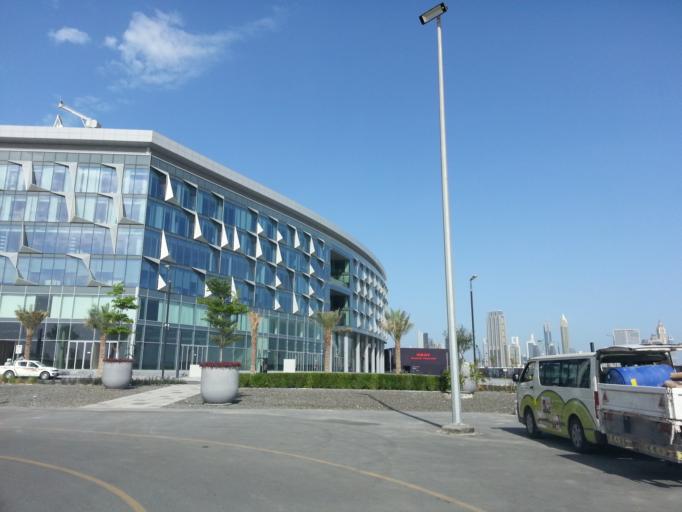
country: AE
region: Dubai
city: Dubai
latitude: 25.1892
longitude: 55.2993
